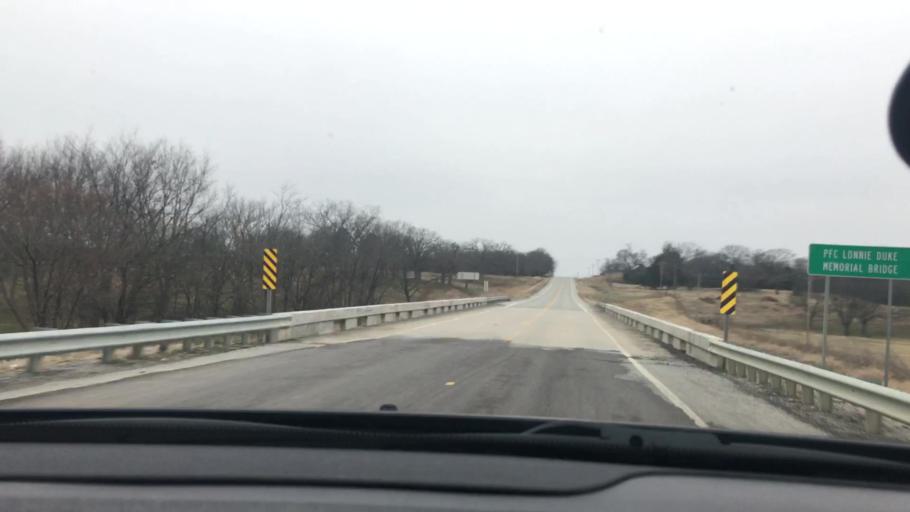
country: US
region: Oklahoma
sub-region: Coal County
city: Coalgate
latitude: 34.5055
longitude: -96.3639
